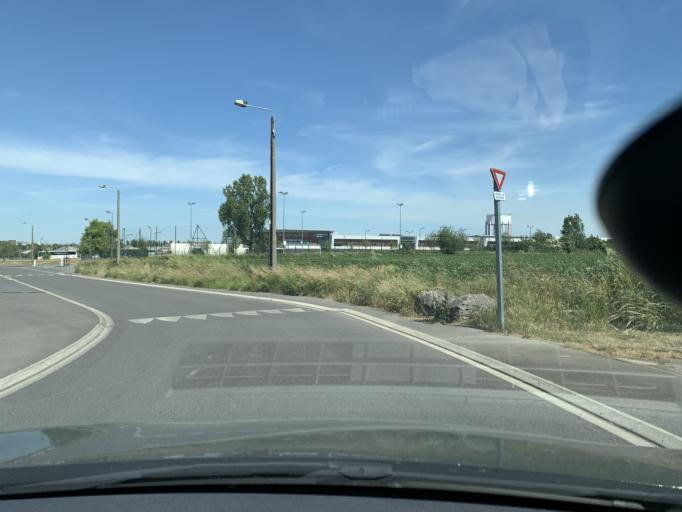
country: FR
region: Nord-Pas-de-Calais
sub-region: Departement du Nord
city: Cambrai
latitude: 50.1585
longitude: 3.2652
